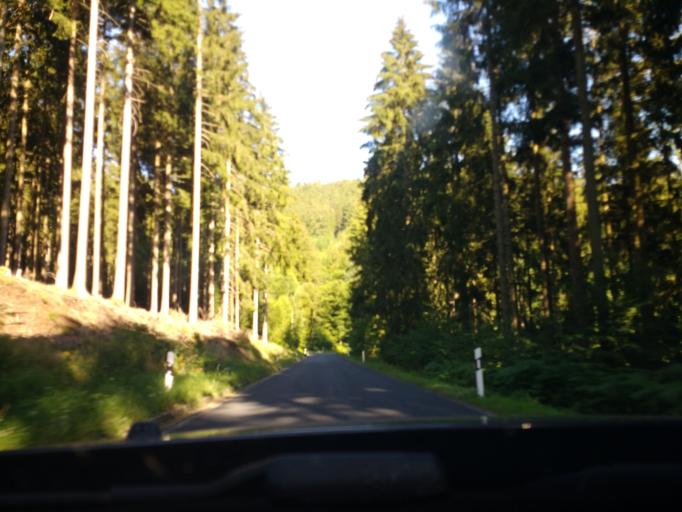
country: DE
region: Rheinland-Pfalz
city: Densborn
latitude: 50.1278
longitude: 6.6294
